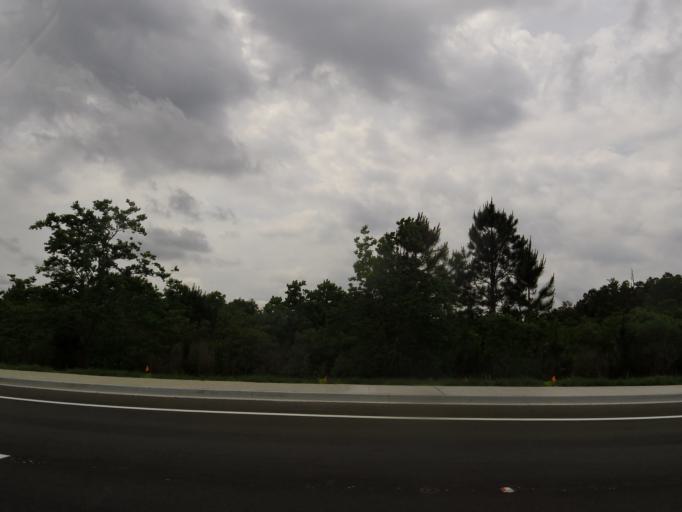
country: US
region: Florida
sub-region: Saint Johns County
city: Villano Beach
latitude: 29.9826
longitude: -81.4640
